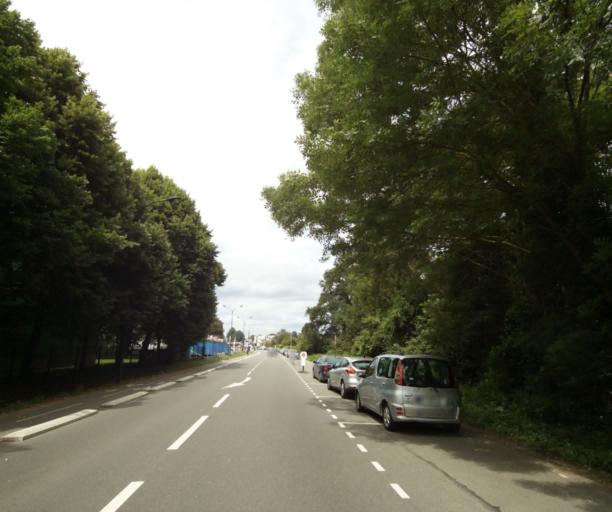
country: FR
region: Ile-de-France
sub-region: Departement des Yvelines
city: Saint-Cyr-l'Ecole
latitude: 48.7925
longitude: 2.0629
